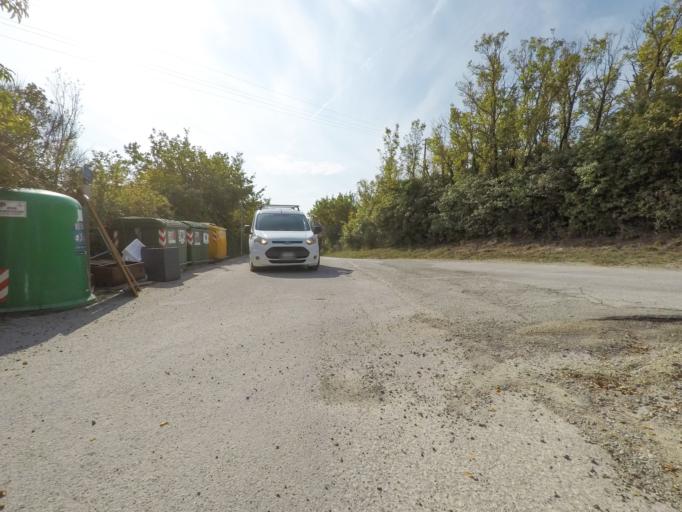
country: IT
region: Tuscany
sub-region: Provincia di Siena
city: Castellina in Chianti
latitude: 43.4277
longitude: 11.3348
